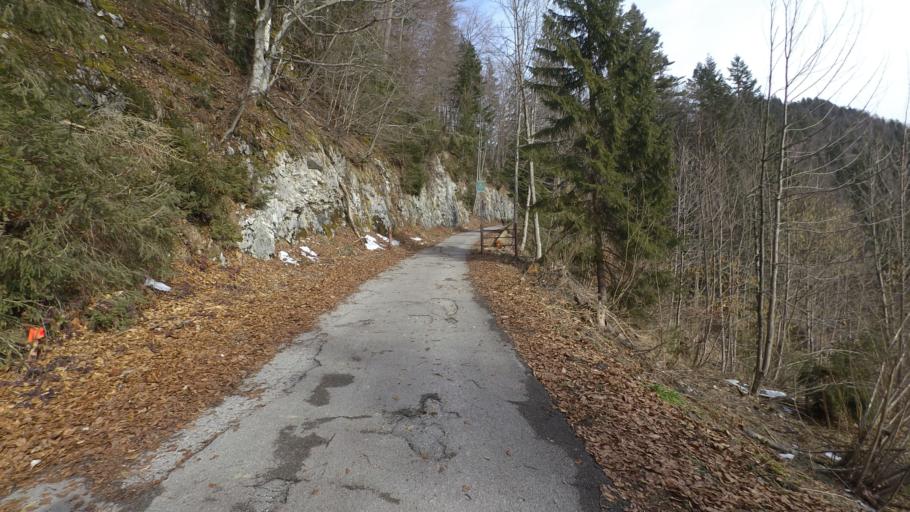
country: DE
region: Bavaria
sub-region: Upper Bavaria
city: Reit im Winkl
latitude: 47.6829
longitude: 12.4473
